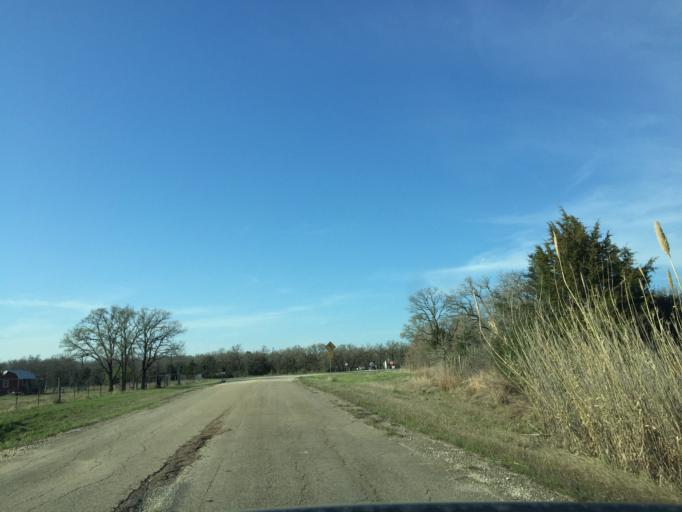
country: US
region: Texas
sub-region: Lee County
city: Lexington
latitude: 30.4659
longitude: -97.1478
